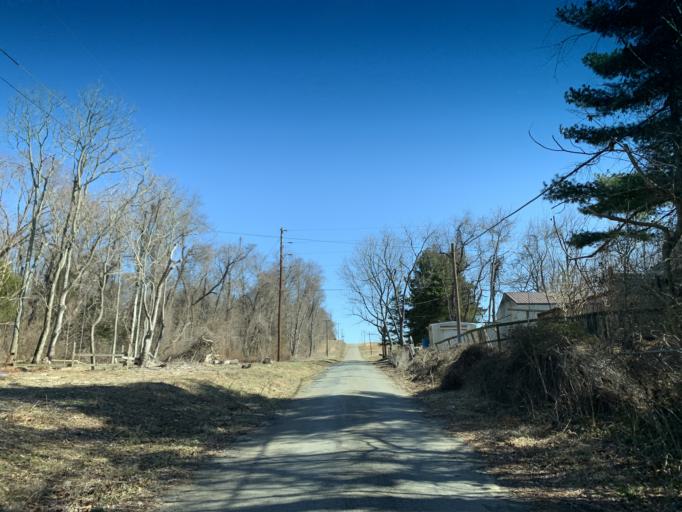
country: US
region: Maryland
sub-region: Cecil County
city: Charlestown
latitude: 39.4473
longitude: -75.9740
